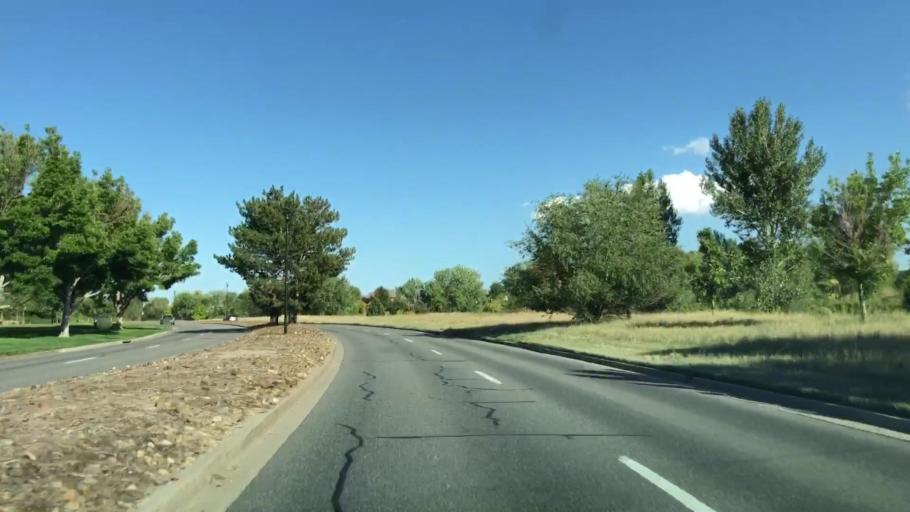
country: US
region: Colorado
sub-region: Arapahoe County
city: Dove Valley
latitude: 39.6104
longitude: -104.8037
